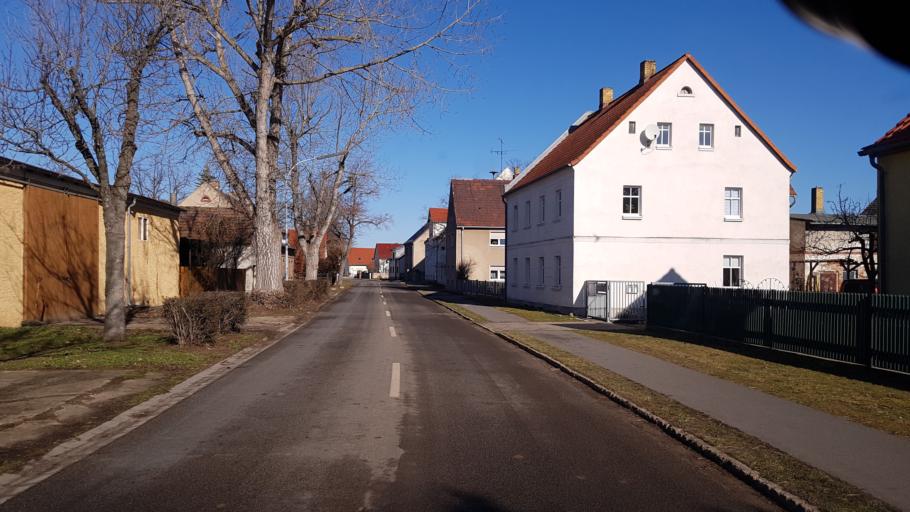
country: DE
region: Saxony
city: Arzberg
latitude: 51.5180
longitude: 13.1853
